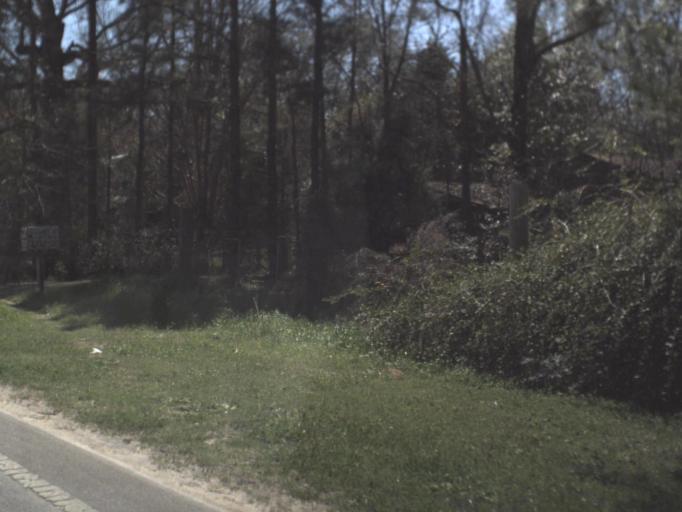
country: US
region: Florida
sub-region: Gadsden County
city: Gretna
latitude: 30.6722
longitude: -84.6153
